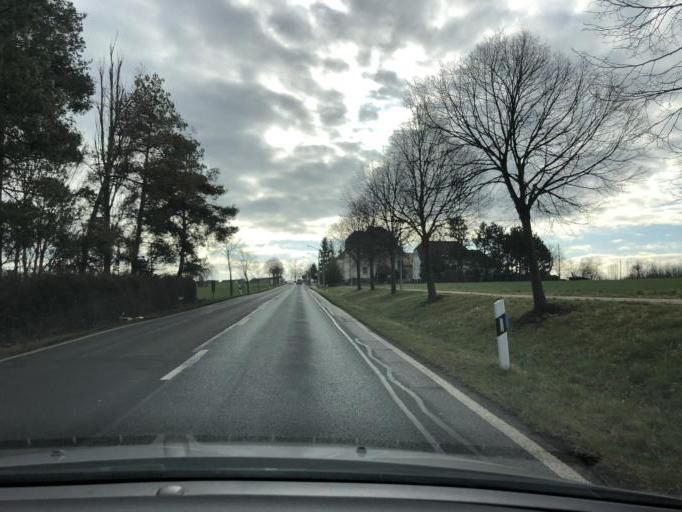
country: DE
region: Saxony
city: Dobeln
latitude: 51.1335
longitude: 13.1072
